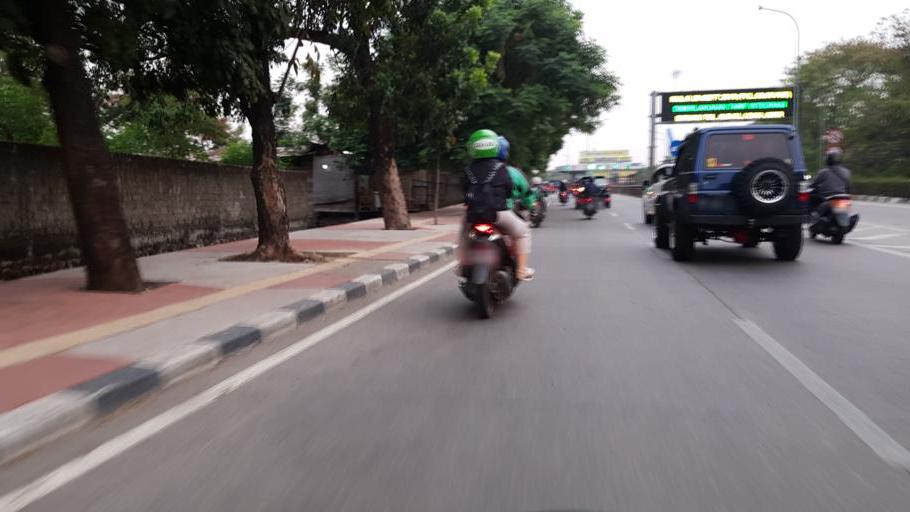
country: ID
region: West Java
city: Cileungsir
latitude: -6.3083
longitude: 106.8968
